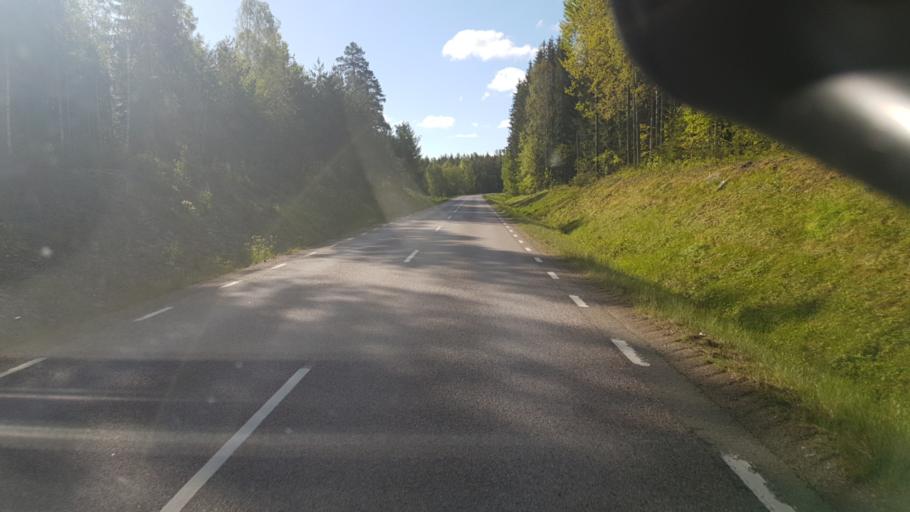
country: SE
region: Vaermland
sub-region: Arvika Kommun
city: Arvika
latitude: 59.5188
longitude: 12.6273
